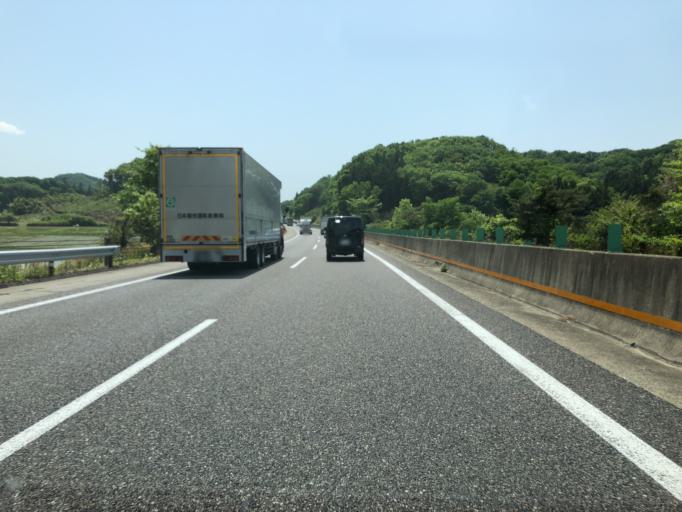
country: JP
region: Fukushima
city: Sukagawa
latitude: 37.1754
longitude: 140.2722
